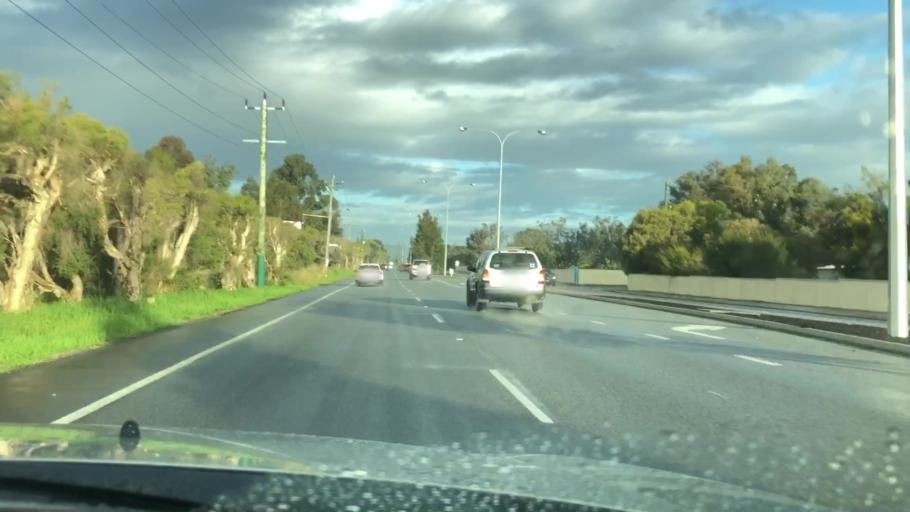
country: AU
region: Western Australia
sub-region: Armadale
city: Harrisdale
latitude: -32.1100
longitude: 115.9418
